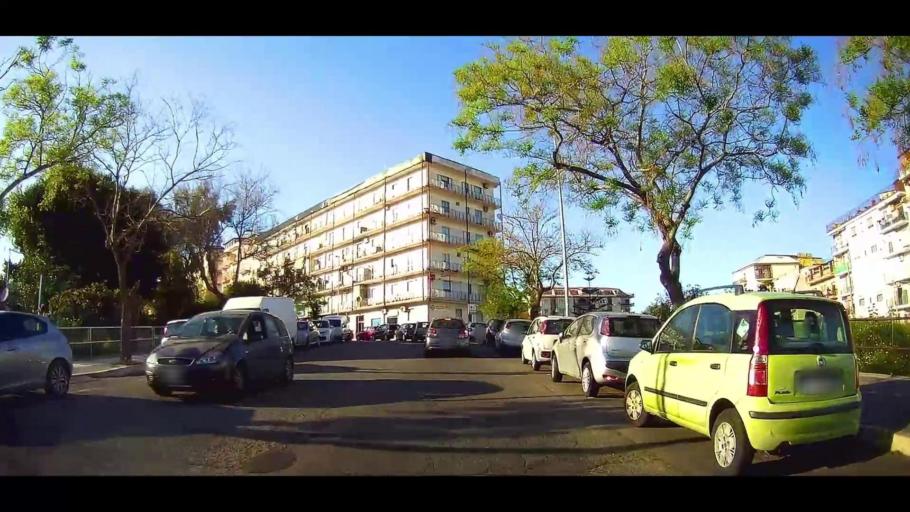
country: IT
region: Calabria
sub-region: Provincia di Crotone
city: Crotone
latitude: 39.0750
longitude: 17.1290
